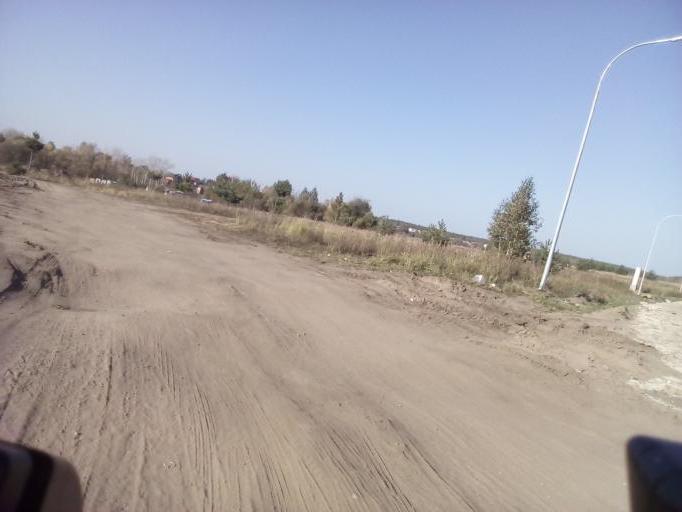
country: RU
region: Moskovskaya
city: Ramenskoye
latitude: 55.5684
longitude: 38.3014
